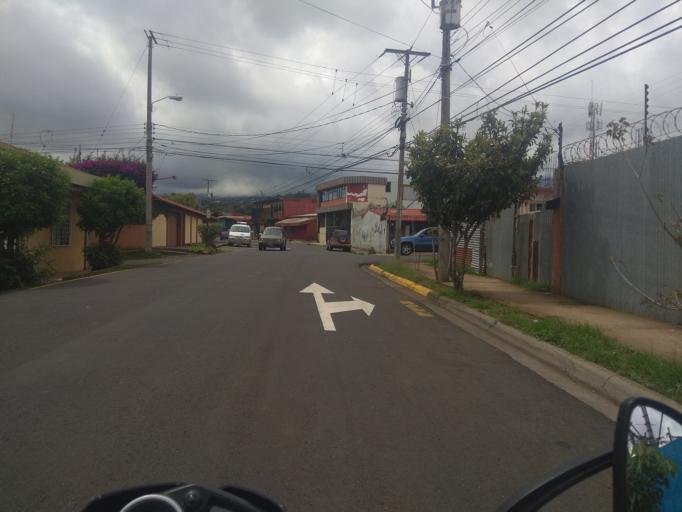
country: CR
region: Heredia
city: San Josecito
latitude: 10.0152
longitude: -84.1028
